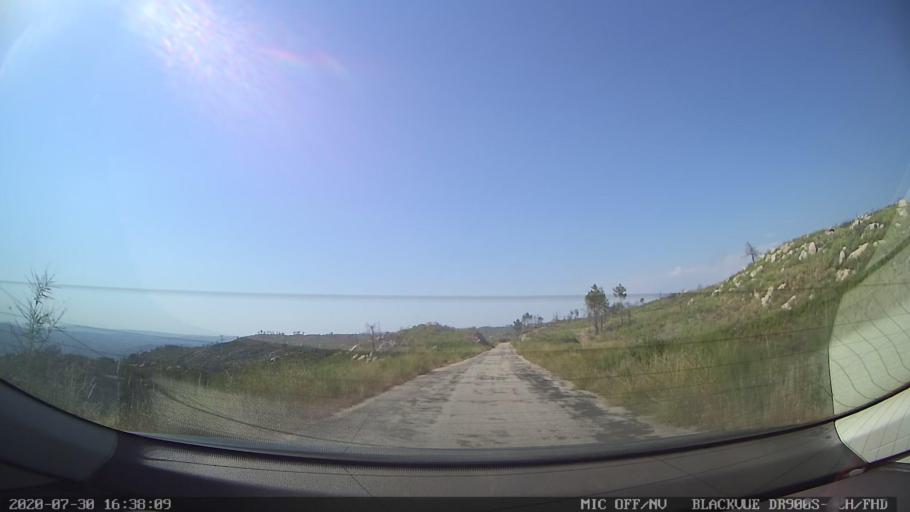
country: PT
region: Vila Real
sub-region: Sabrosa
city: Sabrosa
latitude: 41.3022
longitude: -7.4872
